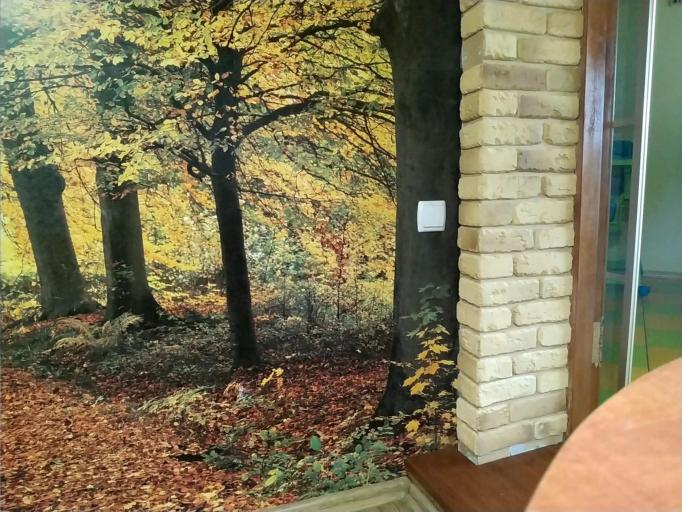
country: RU
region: Smolensk
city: Dorogobuzh
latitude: 54.9094
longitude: 33.3279
